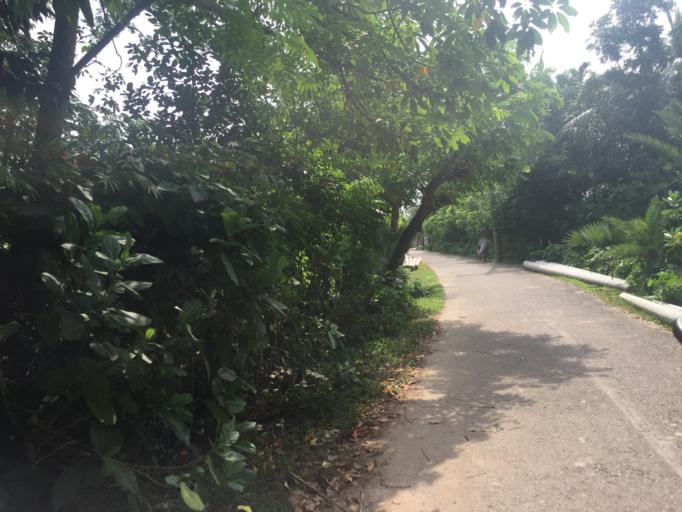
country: BD
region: Barisal
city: Mathba
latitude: 22.2173
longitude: 89.9138
